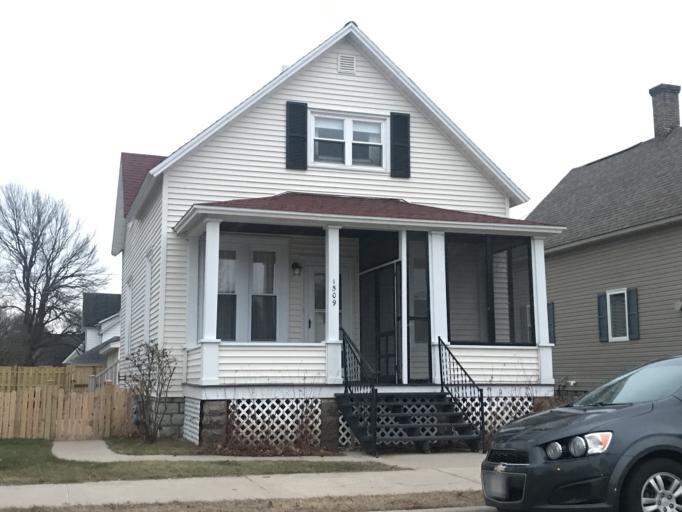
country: US
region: Wisconsin
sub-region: Marinette County
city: Marinette
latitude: 45.0898
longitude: -87.6268
